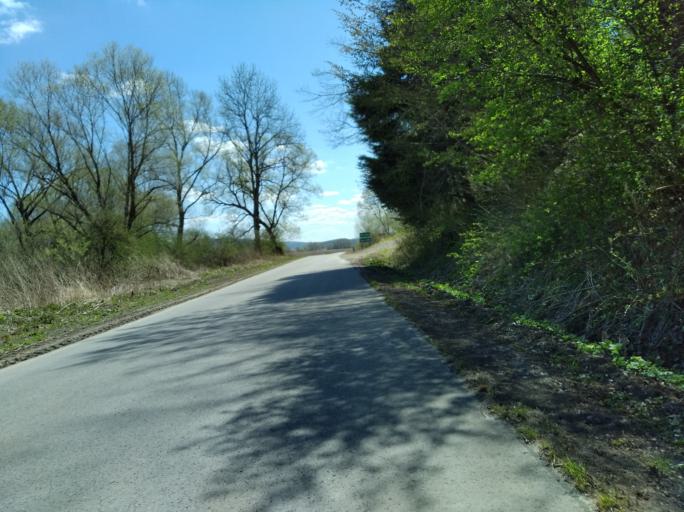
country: PL
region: Subcarpathian Voivodeship
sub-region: Powiat brzozowski
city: Dydnia
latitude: 49.6836
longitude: 22.2400
